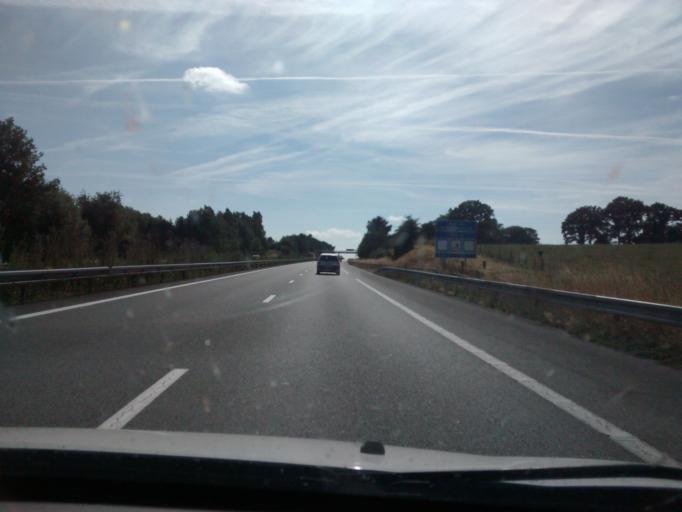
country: FR
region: Pays de la Loire
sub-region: Departement de la Mayenne
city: Loiron
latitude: 48.0781
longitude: -0.9087
